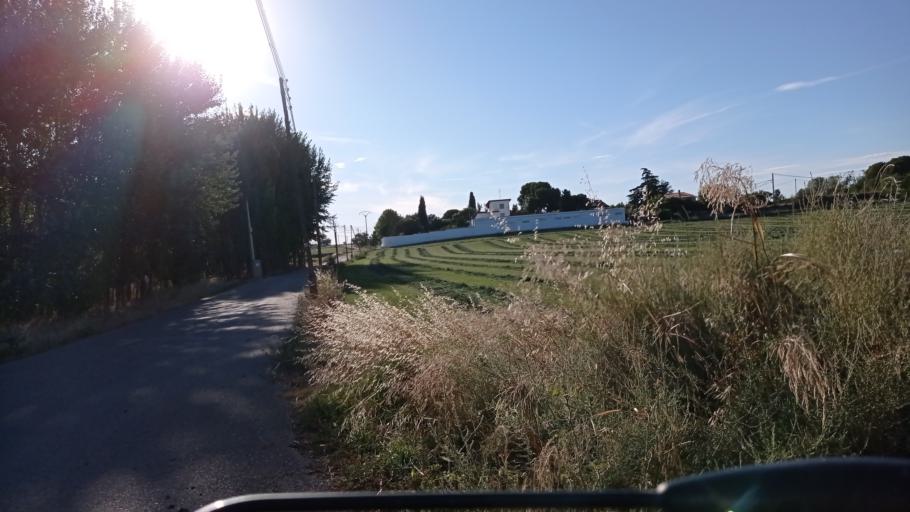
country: ES
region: Aragon
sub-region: Provincia de Zaragoza
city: Oliver-Valdefierro, Oliver, Valdefierro
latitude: 41.6650
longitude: -0.9589
